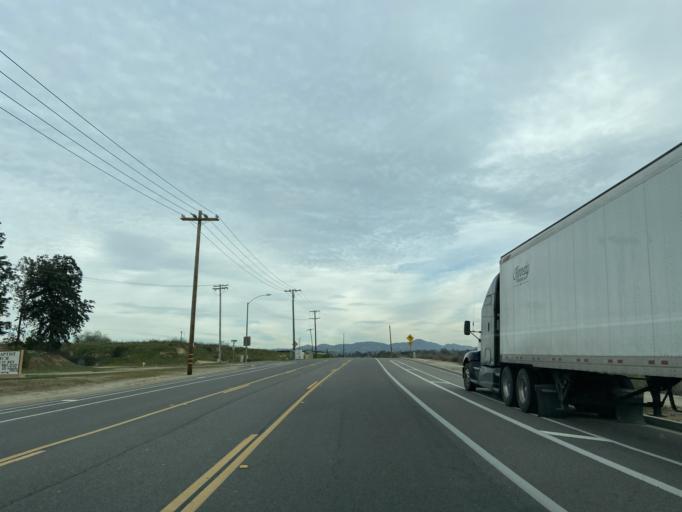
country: US
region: California
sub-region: San Diego County
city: Camp Pendleton North
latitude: 33.2558
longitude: -117.2892
